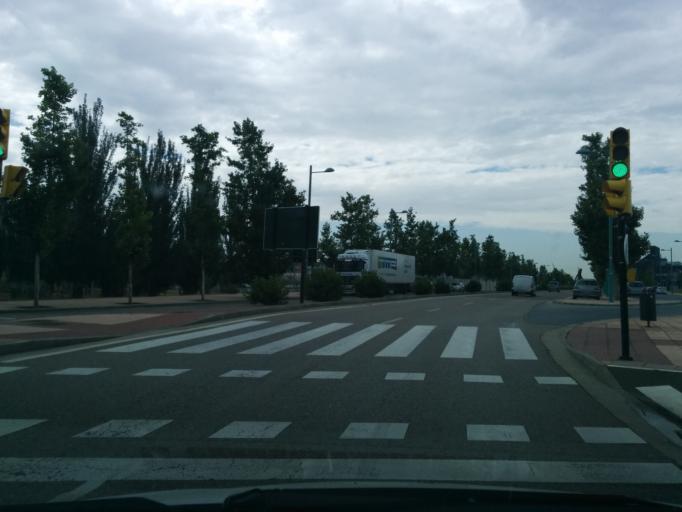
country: ES
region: Aragon
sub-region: Provincia de Zaragoza
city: Almozara
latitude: 41.6785
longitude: -0.8992
